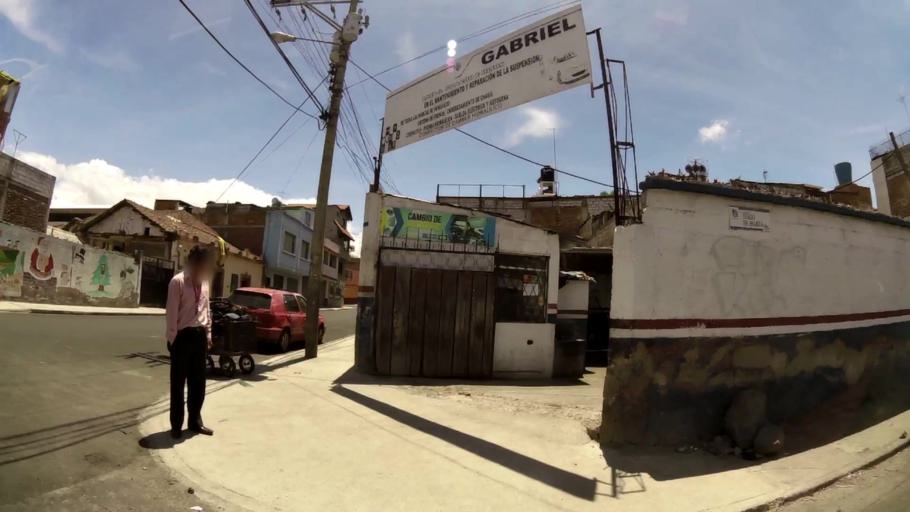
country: EC
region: Chimborazo
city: Riobamba
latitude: -1.6654
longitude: -78.6540
